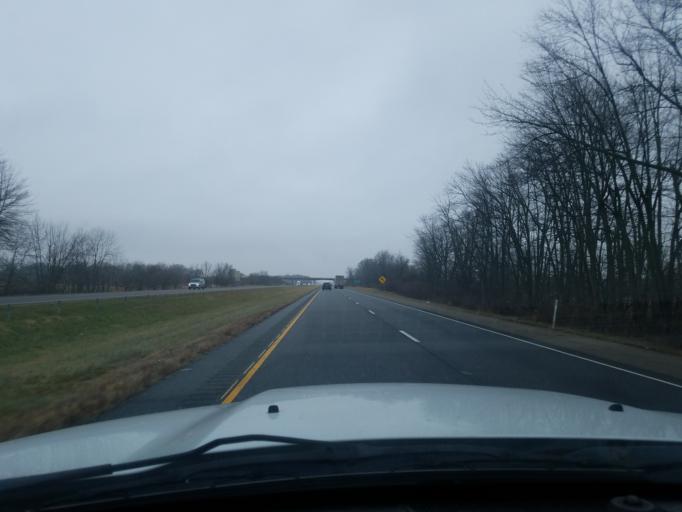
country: US
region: Indiana
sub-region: Madison County
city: Alexandria
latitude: 40.2872
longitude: -85.5580
